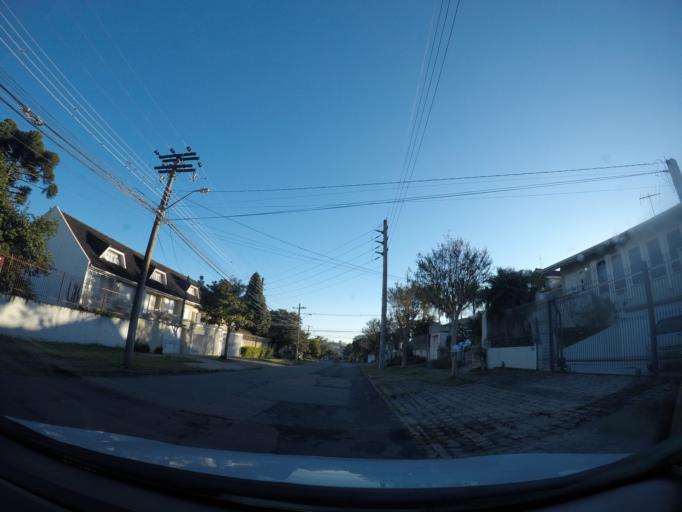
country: BR
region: Parana
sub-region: Curitiba
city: Curitiba
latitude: -25.4193
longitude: -49.2841
